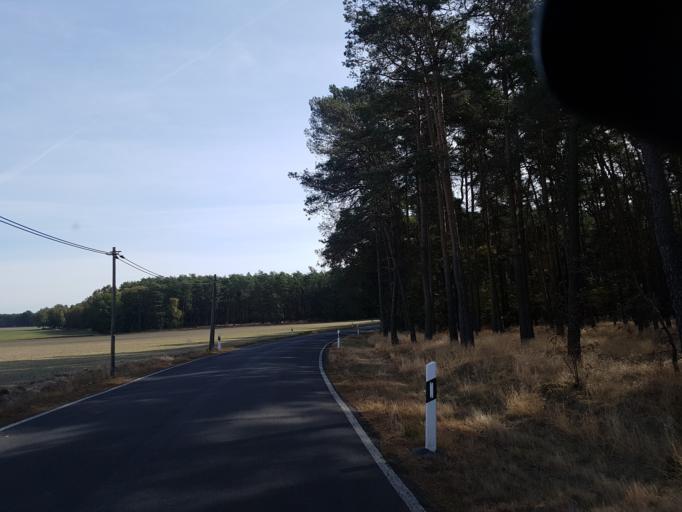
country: DE
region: Brandenburg
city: Schlieben
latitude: 51.6958
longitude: 13.4276
